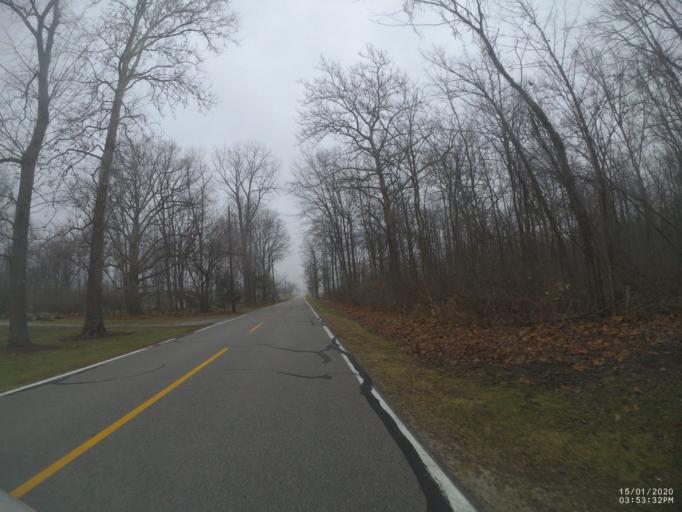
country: US
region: Ohio
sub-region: Wood County
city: Pemberville
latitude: 41.4137
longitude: -83.4095
